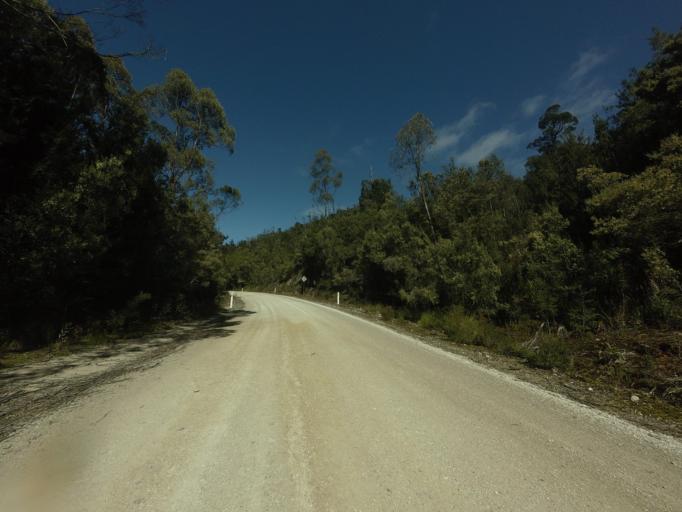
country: AU
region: Tasmania
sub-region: Huon Valley
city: Geeveston
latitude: -42.8286
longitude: 146.3871
